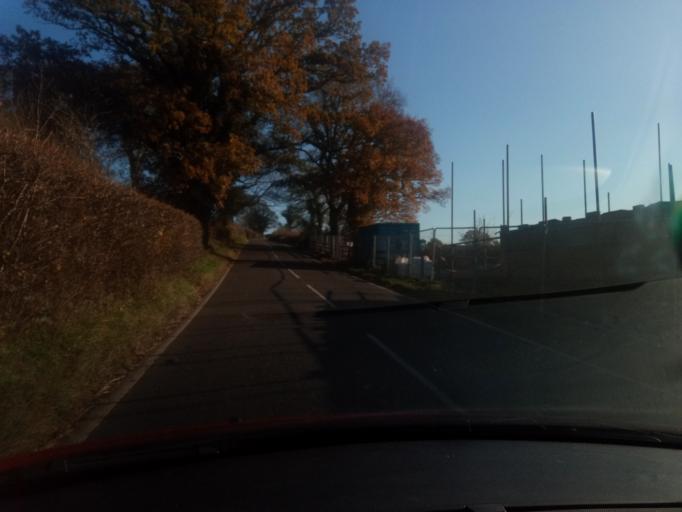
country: GB
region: England
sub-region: Derbyshire
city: Belper
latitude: 53.0225
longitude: -1.5322
